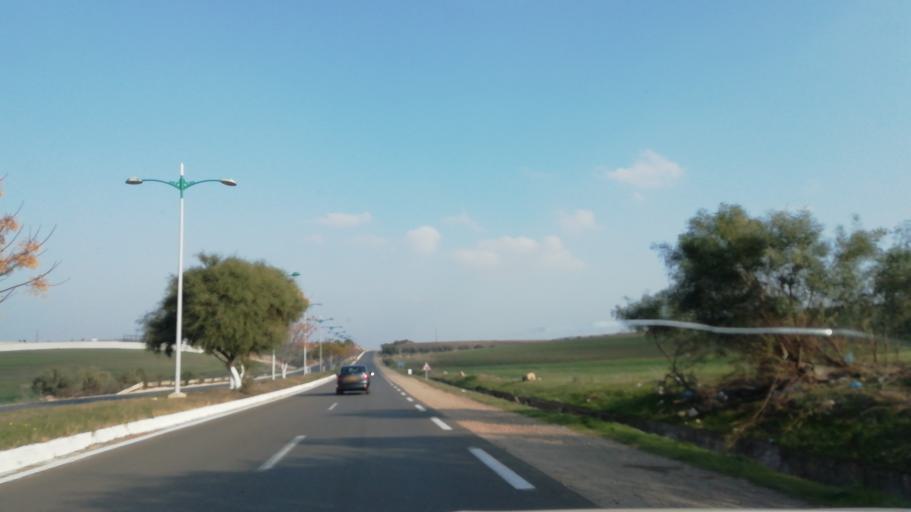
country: DZ
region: Ain Temouchent
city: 'Ain Temouchent
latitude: 35.2929
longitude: -1.1159
